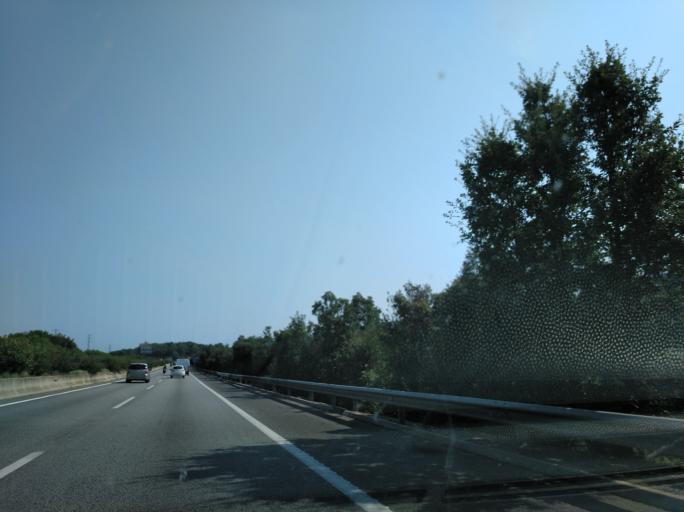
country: ES
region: Catalonia
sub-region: Provincia de Barcelona
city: Argentona
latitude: 41.5680
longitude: 2.3959
